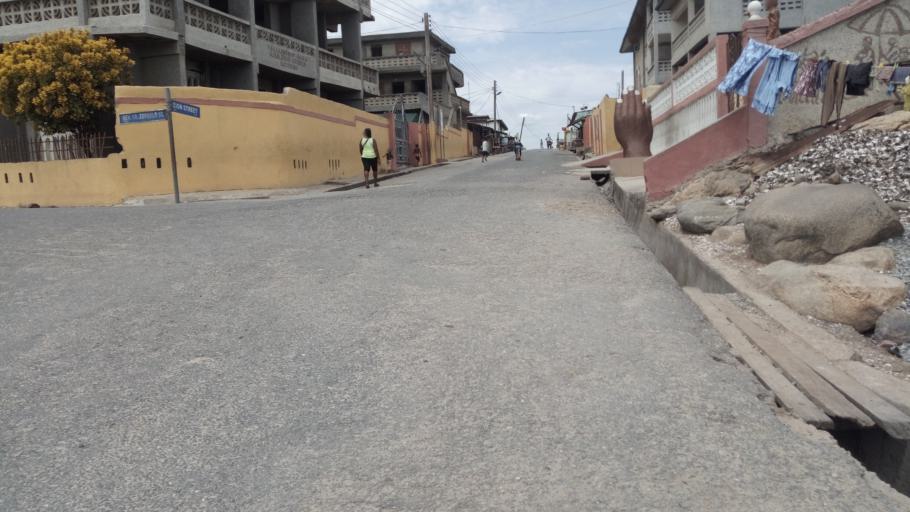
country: GH
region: Central
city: Winneba
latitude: 5.3425
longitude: -0.6222
